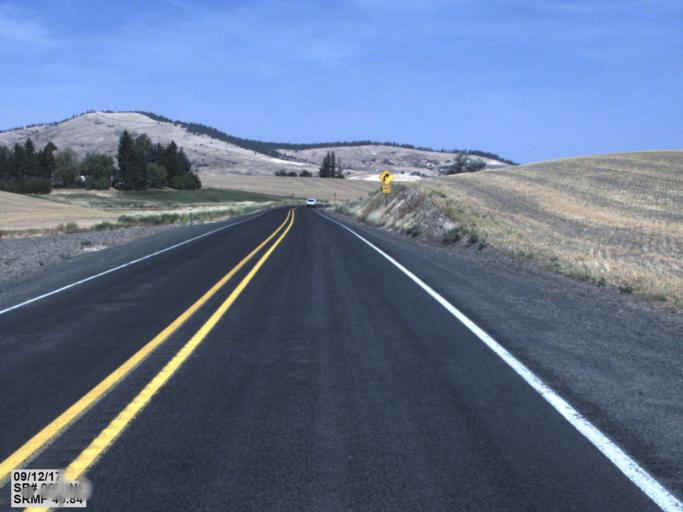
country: US
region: Idaho
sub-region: Benewah County
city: Plummer
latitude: 47.2076
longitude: -117.0884
